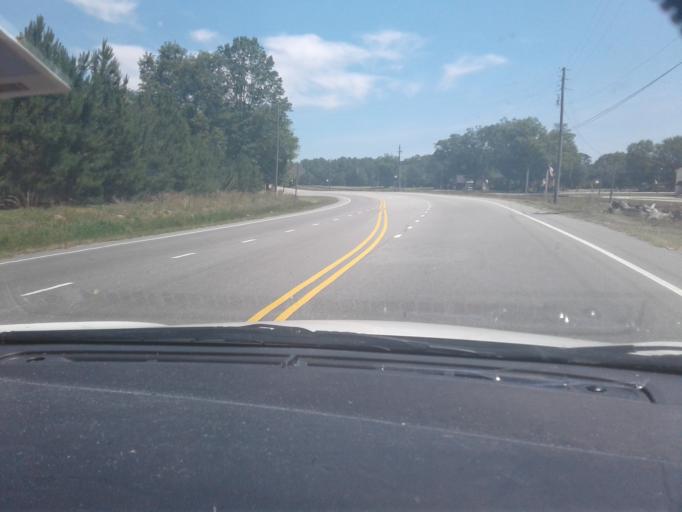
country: US
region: North Carolina
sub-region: Harnett County
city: Lillington
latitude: 35.4784
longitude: -78.8216
